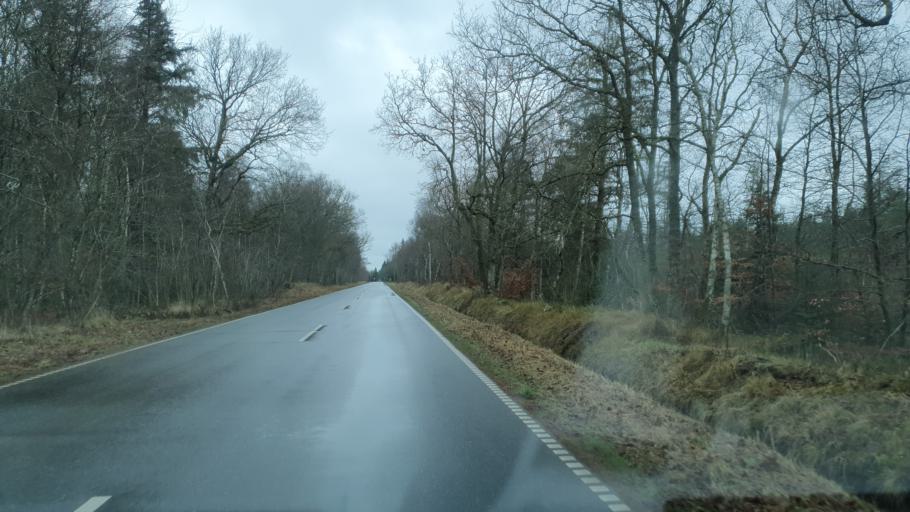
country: DK
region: North Denmark
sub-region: Jammerbugt Kommune
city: Fjerritslev
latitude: 57.1255
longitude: 9.1301
